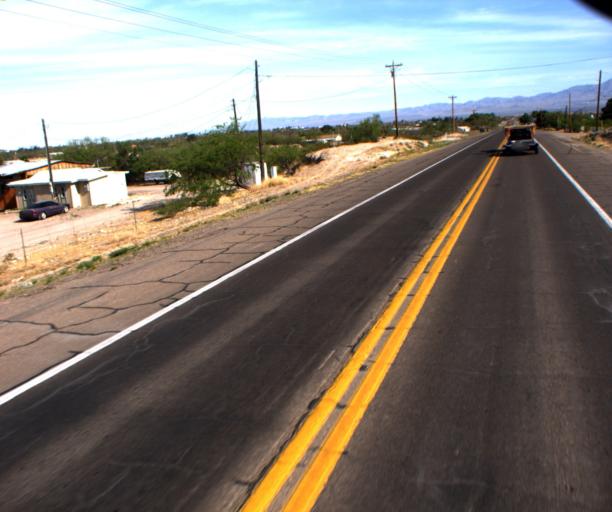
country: US
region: Arizona
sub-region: Graham County
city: Cactus Flat
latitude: 32.7545
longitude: -109.7163
